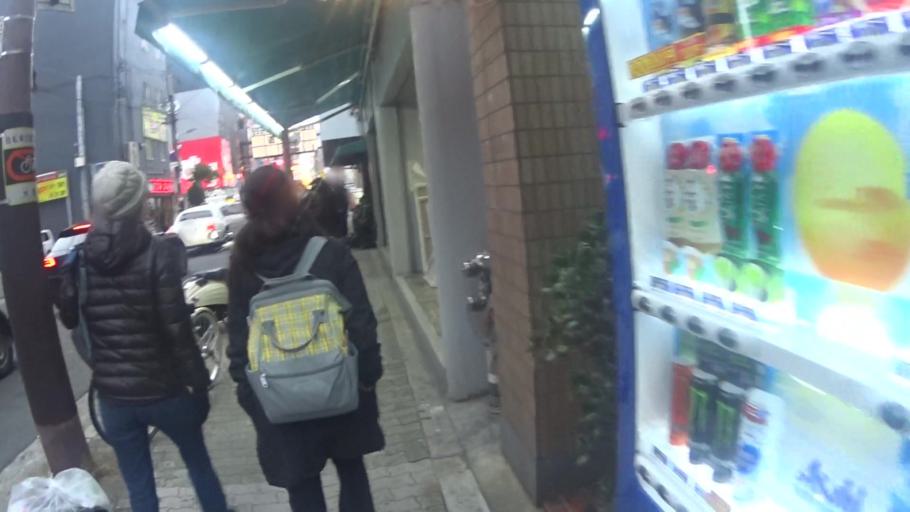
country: JP
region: Osaka
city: Osaka-shi
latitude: 34.6673
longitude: 135.5066
